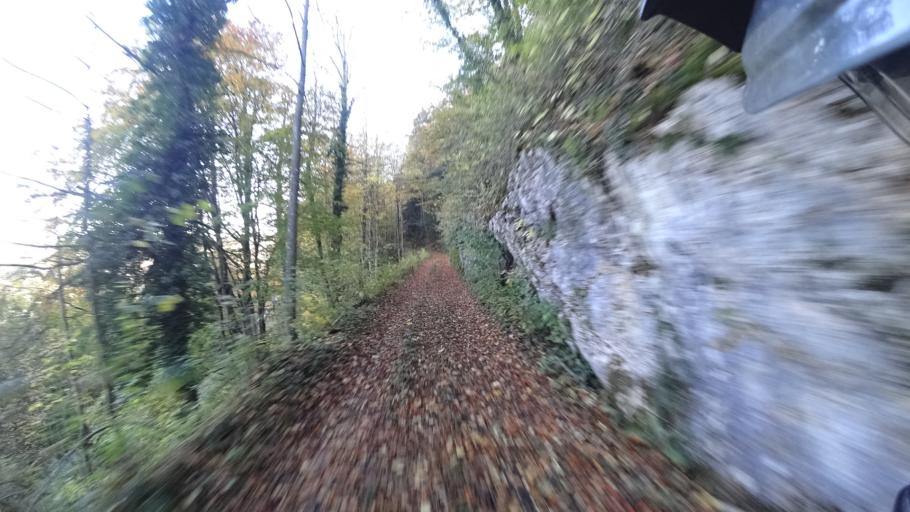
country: HR
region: Karlovacka
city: Plaski
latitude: 44.9627
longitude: 15.4424
